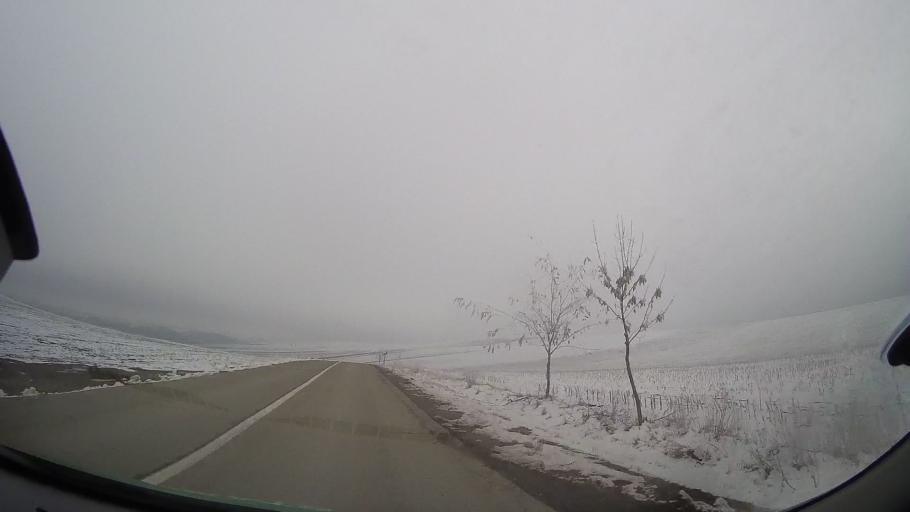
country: RO
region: Vaslui
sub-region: Comuna Ivesti
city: Ivesti
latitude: 46.2038
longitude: 27.5079
